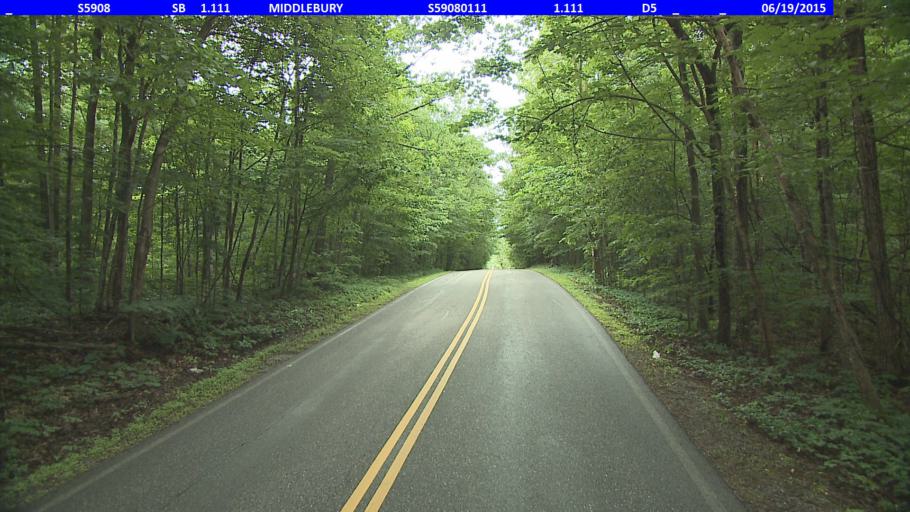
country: US
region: Vermont
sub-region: Addison County
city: Middlebury (village)
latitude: 44.0106
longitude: -73.1401
